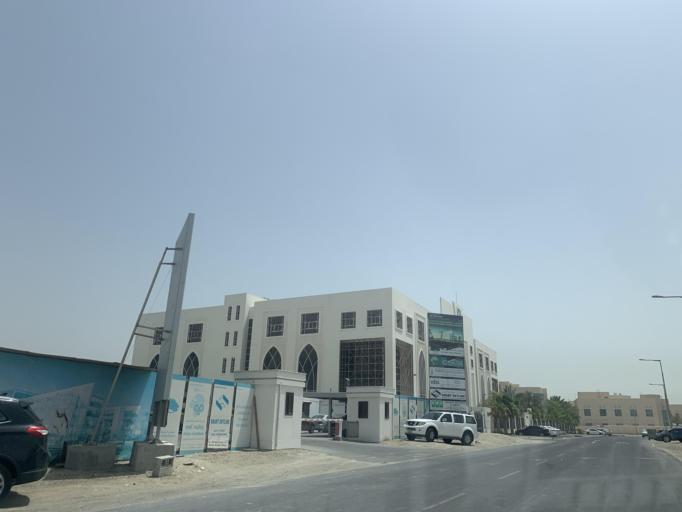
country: BH
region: Northern
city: Madinat `Isa
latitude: 26.1559
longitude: 50.5272
